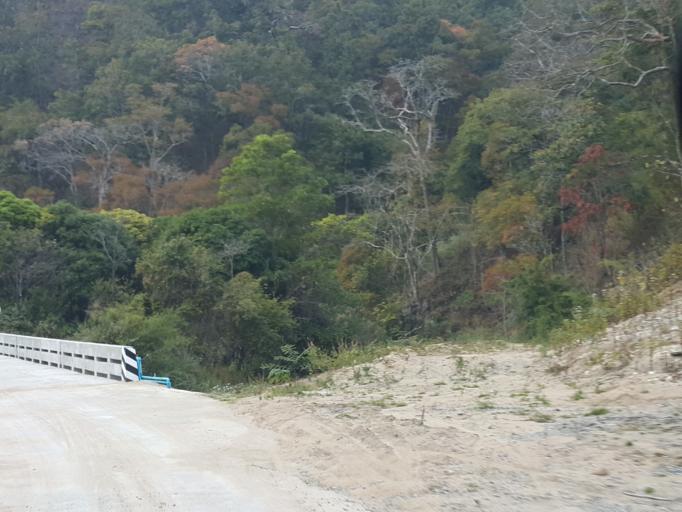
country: TH
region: Chiang Mai
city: Om Koi
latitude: 17.7969
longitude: 98.3081
